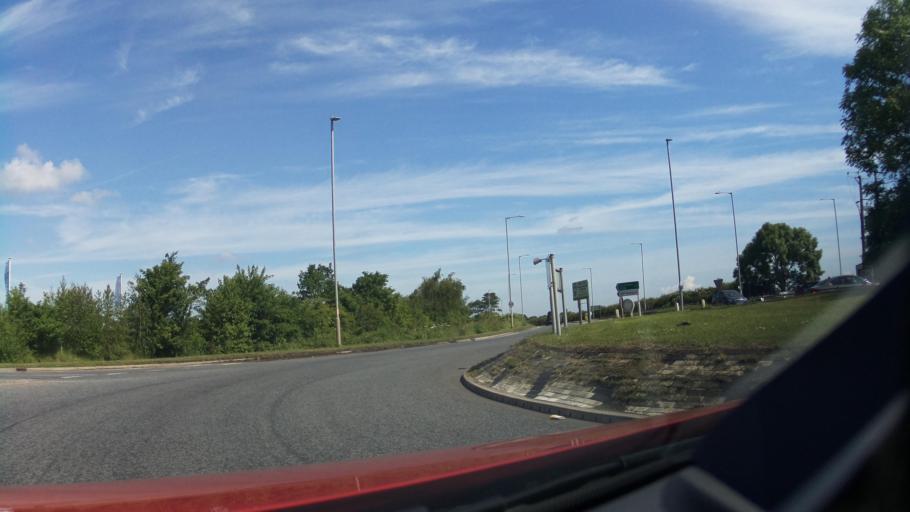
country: GB
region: England
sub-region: Lincolnshire
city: Burton
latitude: 53.2910
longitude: -0.5414
